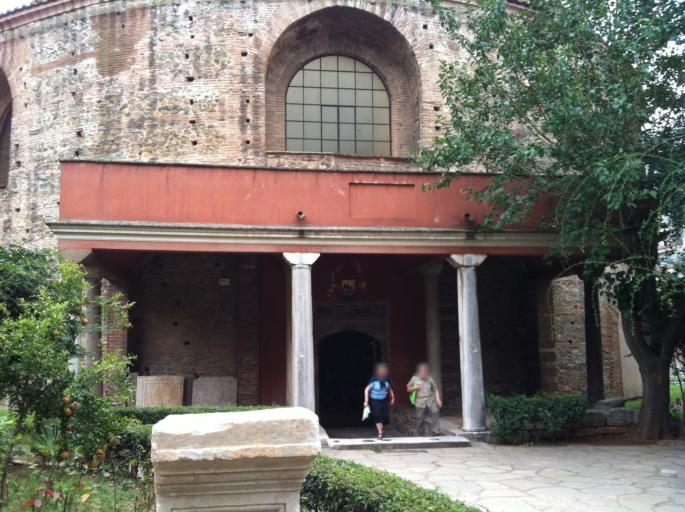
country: GR
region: Central Macedonia
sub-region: Nomos Thessalonikis
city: Agios Pavlos
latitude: 40.6336
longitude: 22.9525
